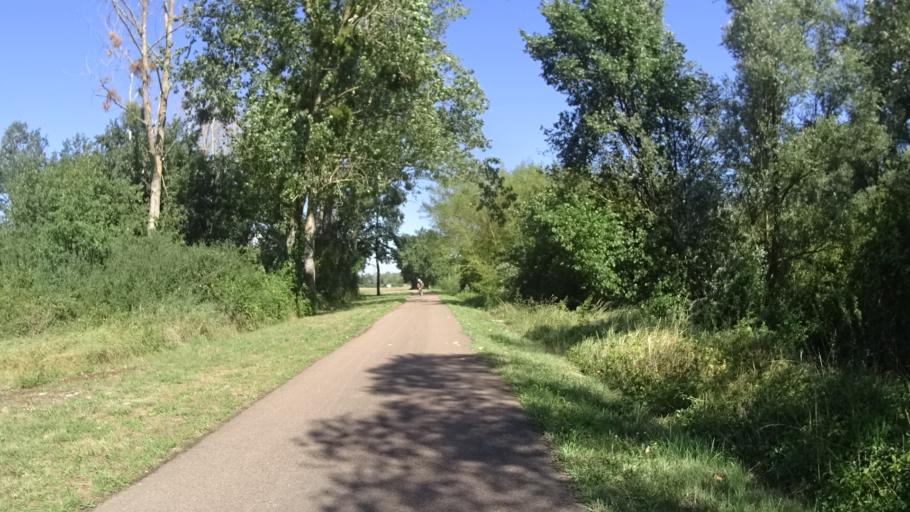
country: FR
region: Bourgogne
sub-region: Departement de la Nievre
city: Neuvy-sur-Loire
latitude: 47.4943
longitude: 2.8901
